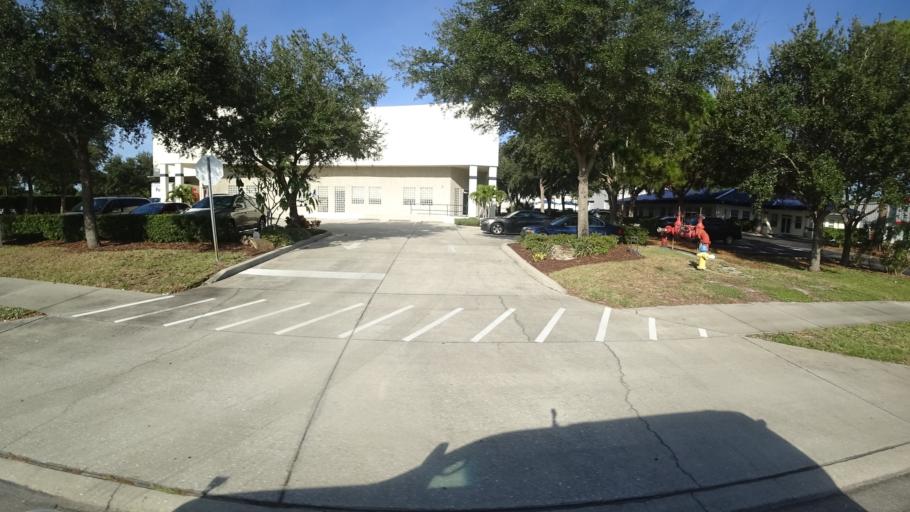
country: US
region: Florida
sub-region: Manatee County
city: Whitfield
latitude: 27.4069
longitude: -82.5567
